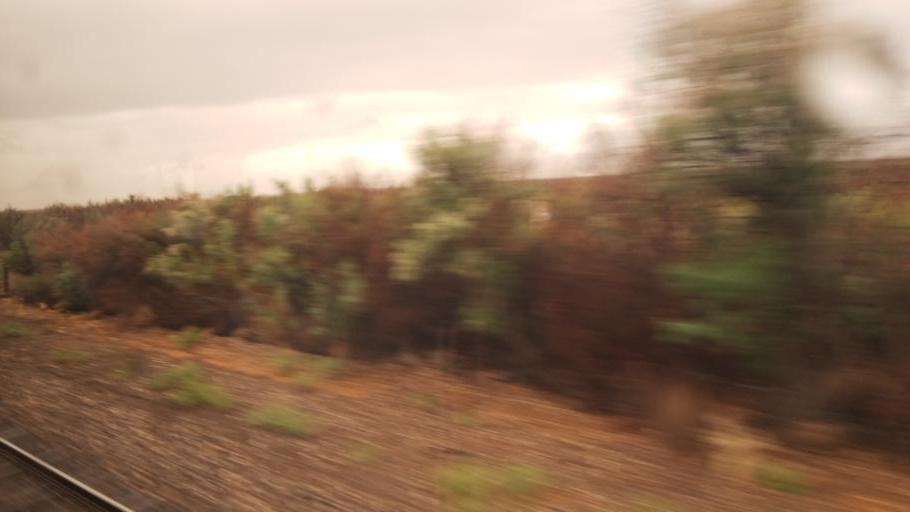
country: US
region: Arizona
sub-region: Navajo County
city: Winslow
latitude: 34.9811
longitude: -110.5575
